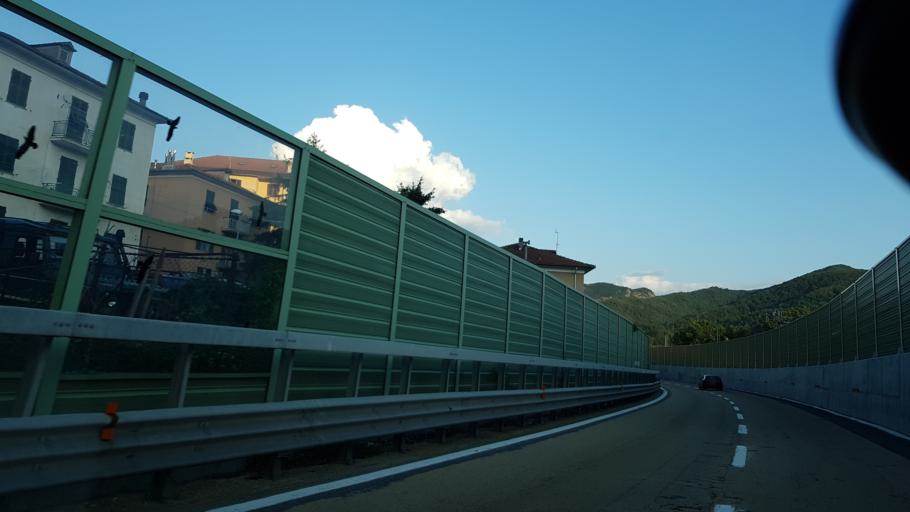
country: IT
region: Liguria
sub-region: Provincia di Genova
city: Ronco Scrivia
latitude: 44.6165
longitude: 8.9484
